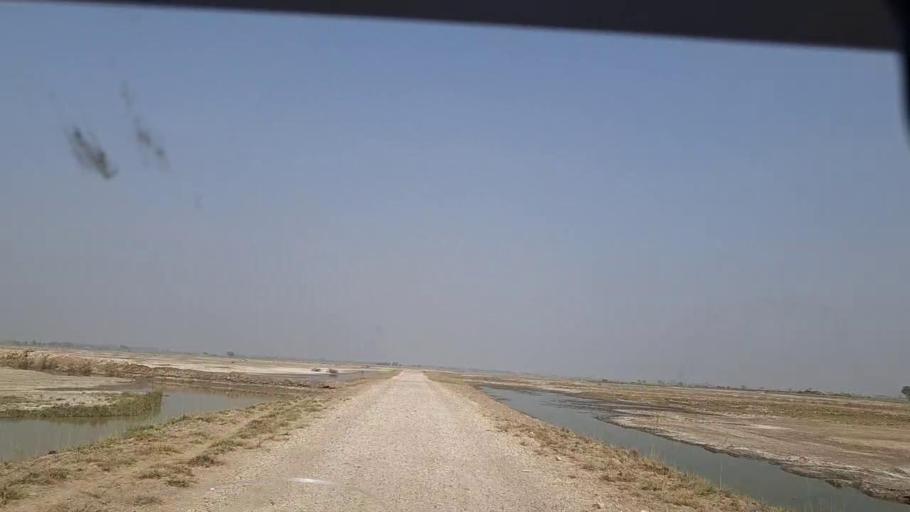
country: PK
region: Sindh
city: Shikarpur
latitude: 28.0466
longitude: 68.6532
